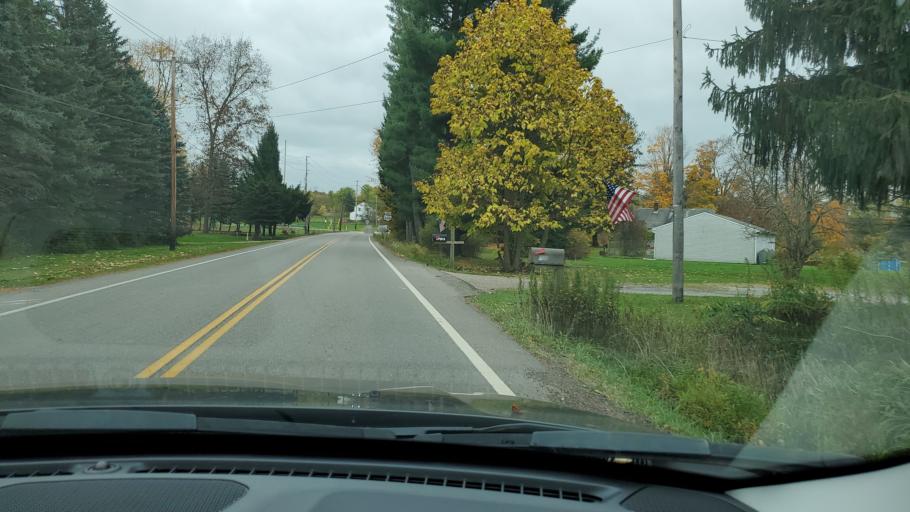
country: US
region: Ohio
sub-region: Mahoning County
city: New Middletown
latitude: 40.9452
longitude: -80.6365
